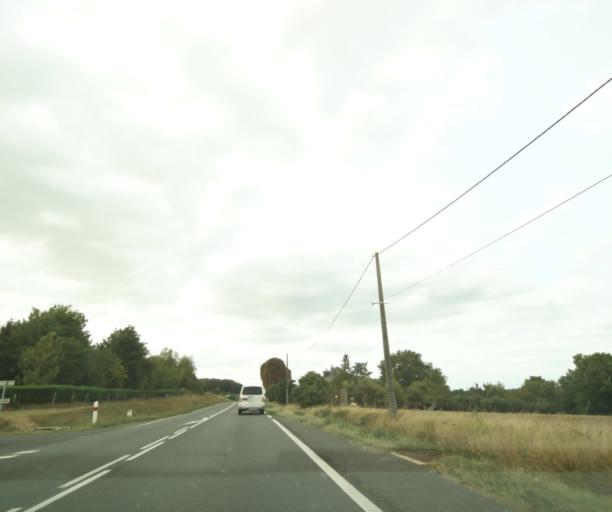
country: FR
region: Centre
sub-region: Departement d'Indre-et-Loire
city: Chambourg-sur-Indre
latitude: 47.1633
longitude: 0.9870
